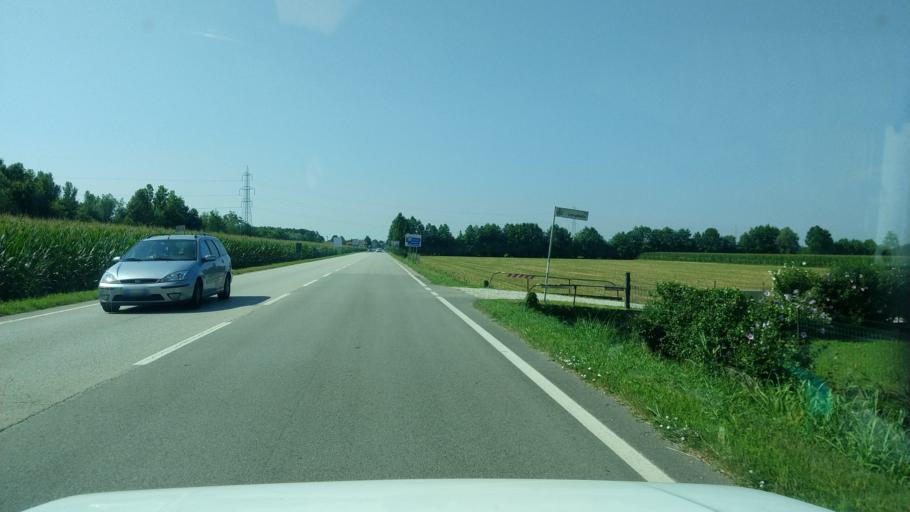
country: IT
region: Veneto
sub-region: Provincia di Vicenza
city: Bressanvido
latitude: 45.6721
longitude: 11.6367
